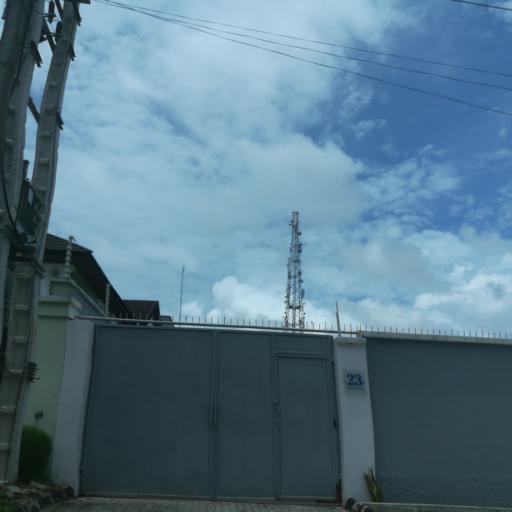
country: NG
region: Lagos
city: Ikoyi
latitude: 6.4417
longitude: 3.4650
